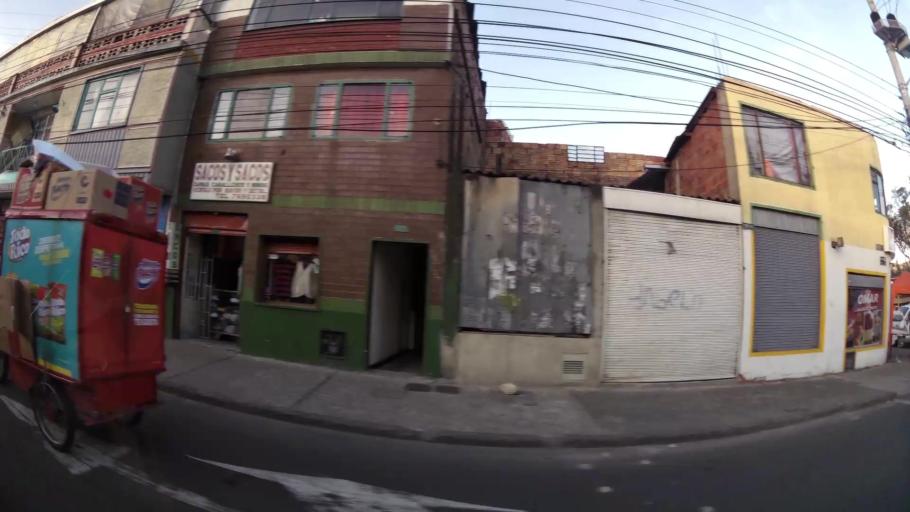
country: CO
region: Bogota D.C.
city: Bogota
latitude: 4.5675
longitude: -74.1303
